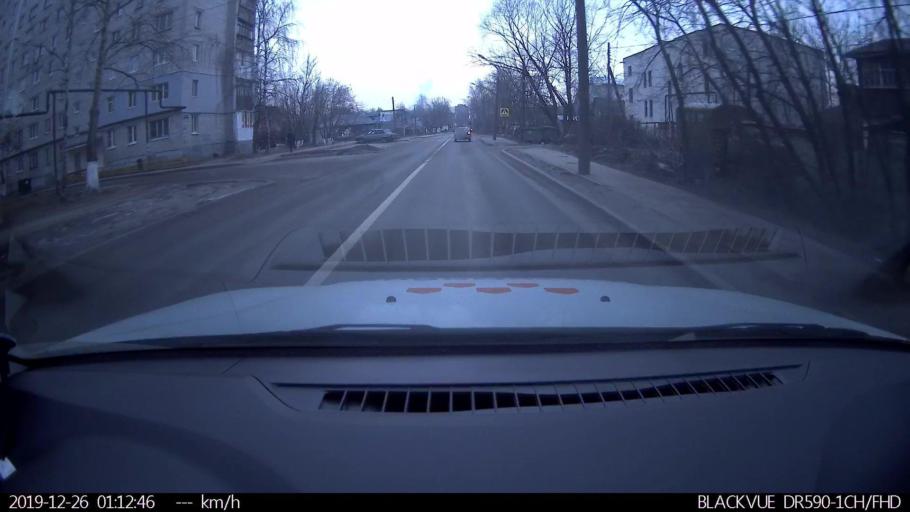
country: RU
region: Nizjnij Novgorod
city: Nizhniy Novgorod
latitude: 56.2819
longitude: 43.9141
